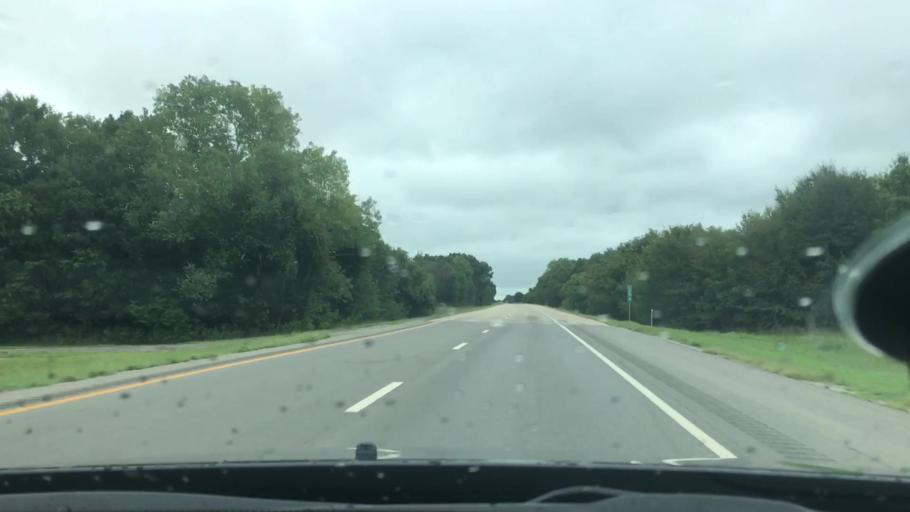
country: US
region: Oklahoma
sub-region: Okmulgee County
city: Morris
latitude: 35.4499
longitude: -95.7382
